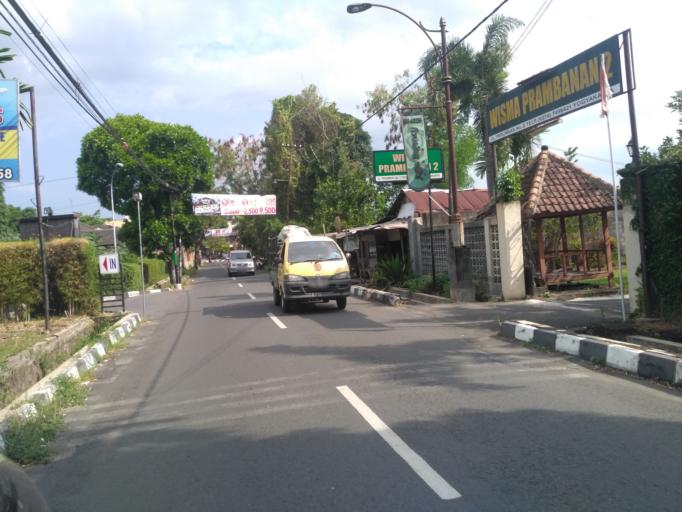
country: ID
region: Daerah Istimewa Yogyakarta
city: Depok
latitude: -7.7821
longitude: 110.4055
